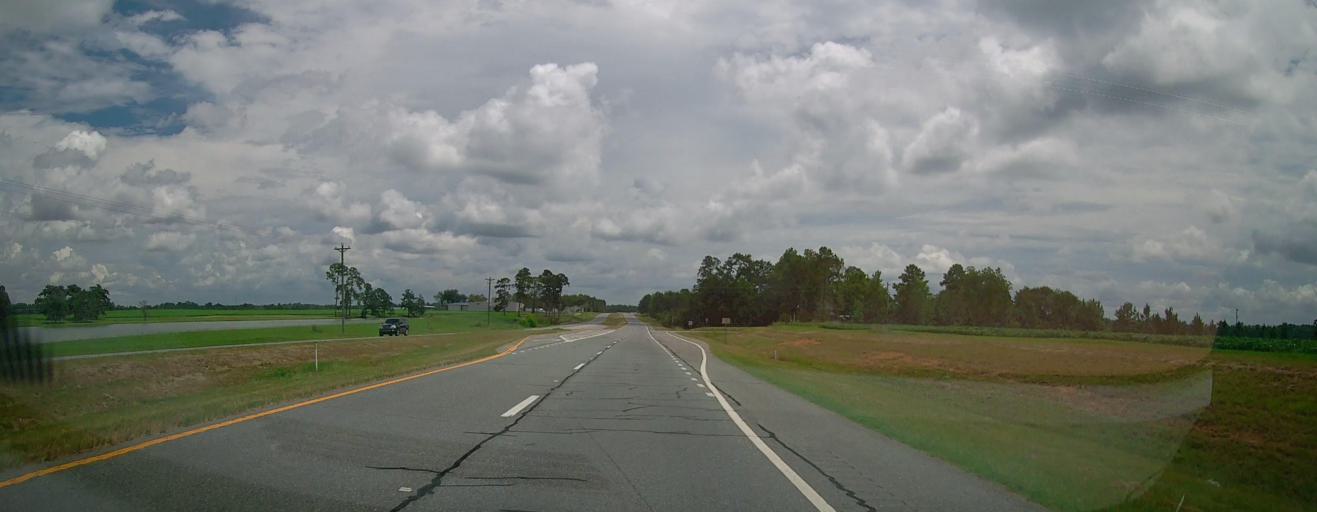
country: US
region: Georgia
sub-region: Pulaski County
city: Hawkinsville
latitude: 32.2218
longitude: -83.3555
